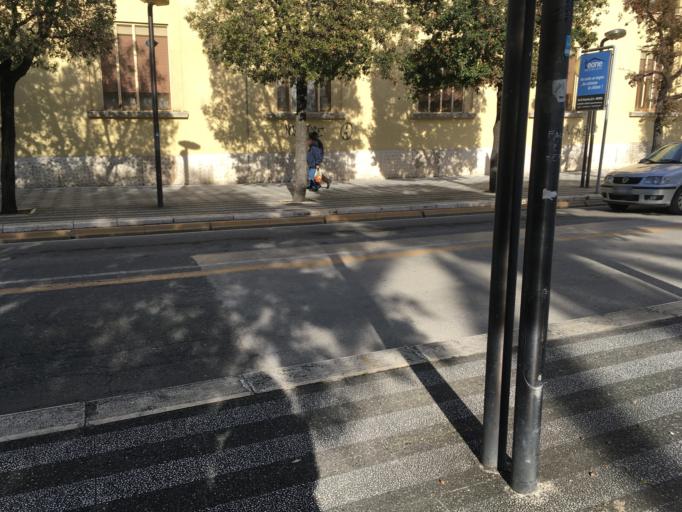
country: IT
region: Apulia
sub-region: Provincia di Barletta - Andria - Trani
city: Andria
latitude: 41.2307
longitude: 16.3035
